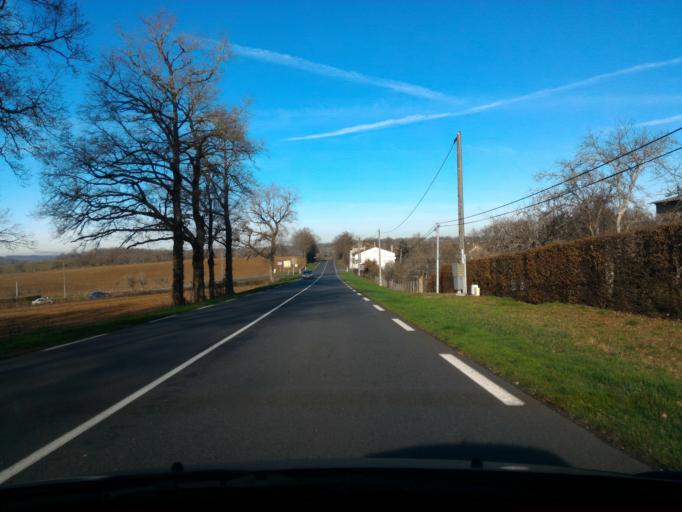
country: FR
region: Poitou-Charentes
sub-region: Departement de la Charente
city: Etagnac
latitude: 45.9191
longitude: 0.7447
